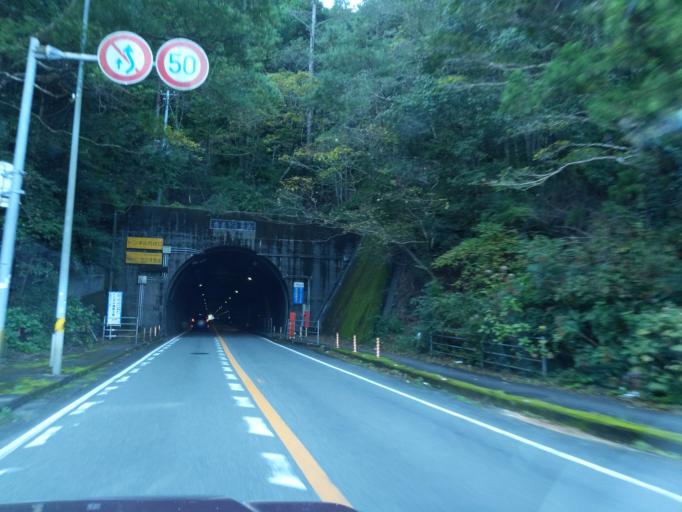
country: JP
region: Kochi
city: Muroto-misakicho
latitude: 33.5571
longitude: 134.3079
